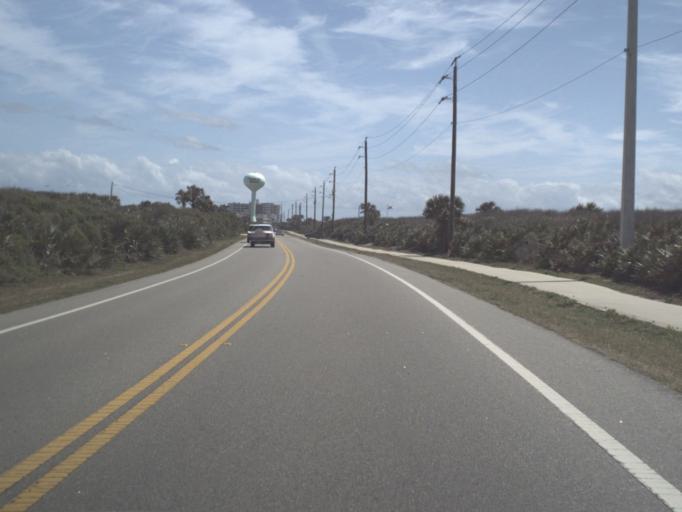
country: US
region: Florida
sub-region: Flagler County
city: Flagler Beach
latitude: 29.4407
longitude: -81.1095
